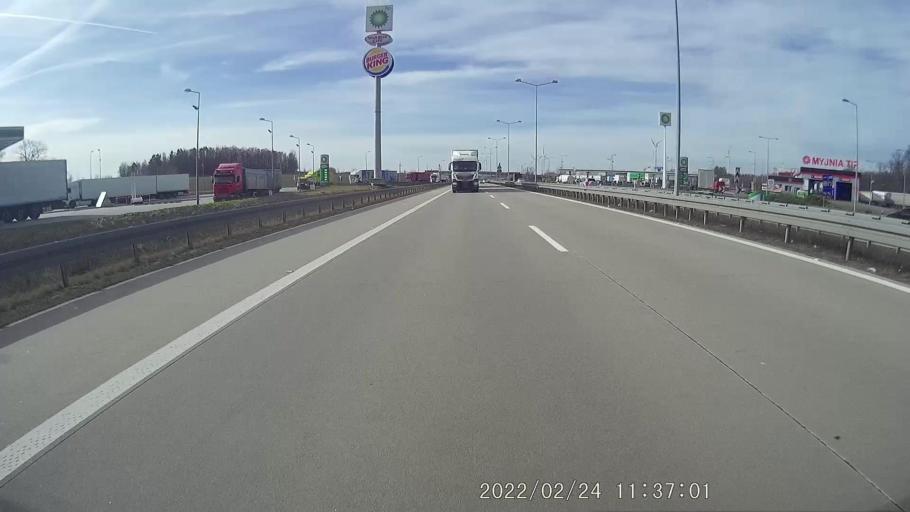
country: PL
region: Lower Silesian Voivodeship
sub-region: Powiat polkowicki
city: Przemkow
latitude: 51.5214
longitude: 15.8171
